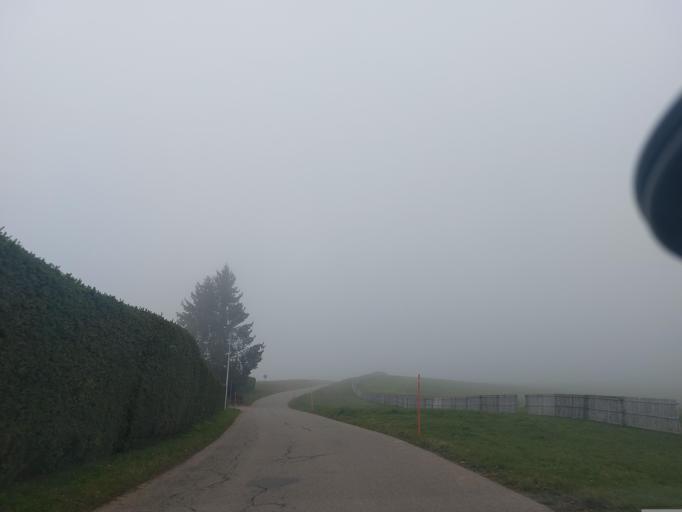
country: CH
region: Vaud
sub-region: Lavaux-Oron District
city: Oron-la-ville
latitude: 46.5779
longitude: 6.8674
